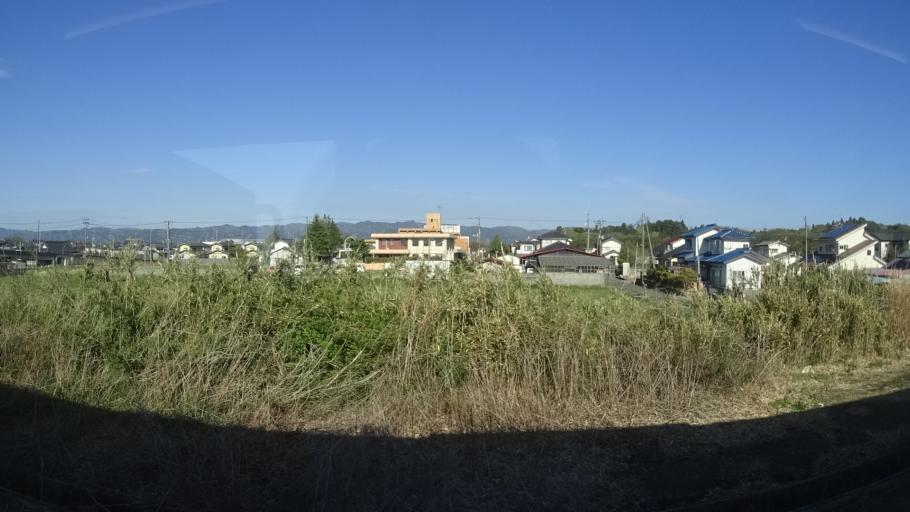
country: JP
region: Fukushima
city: Namie
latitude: 37.5664
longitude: 140.9969
